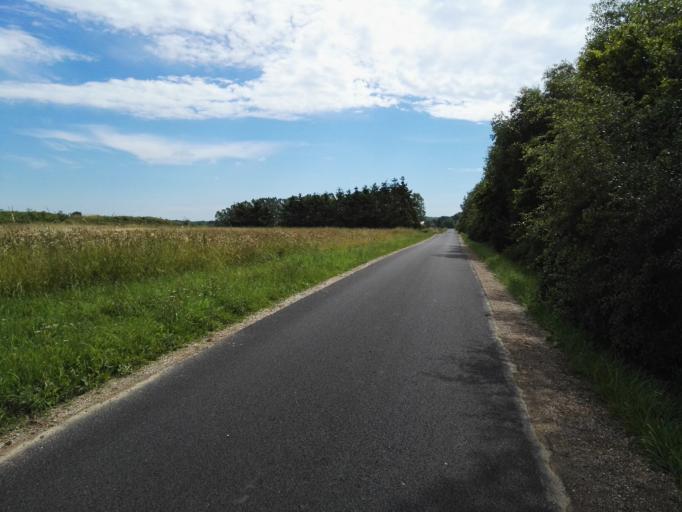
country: DK
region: Capital Region
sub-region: Egedal Kommune
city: Olstykke
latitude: 55.8120
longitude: 12.1699
